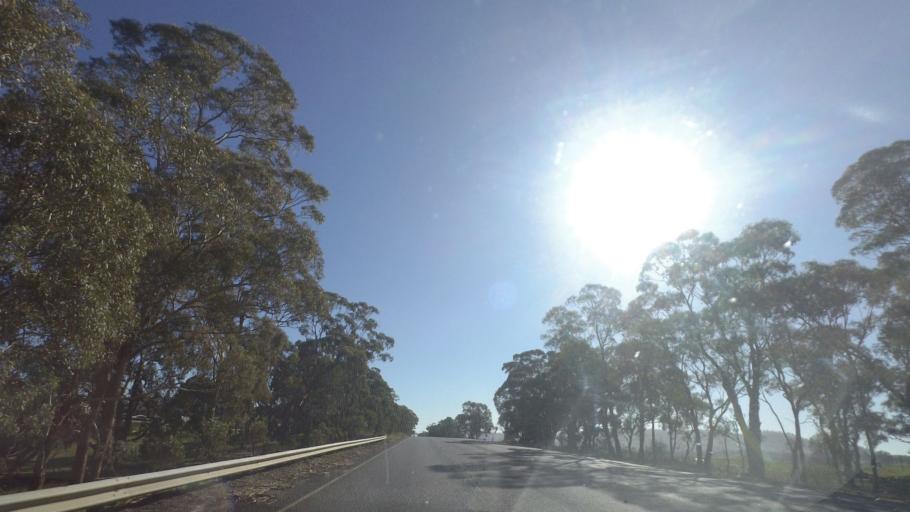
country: AU
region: Victoria
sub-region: Mount Alexander
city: Castlemaine
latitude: -37.0591
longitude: 144.2960
